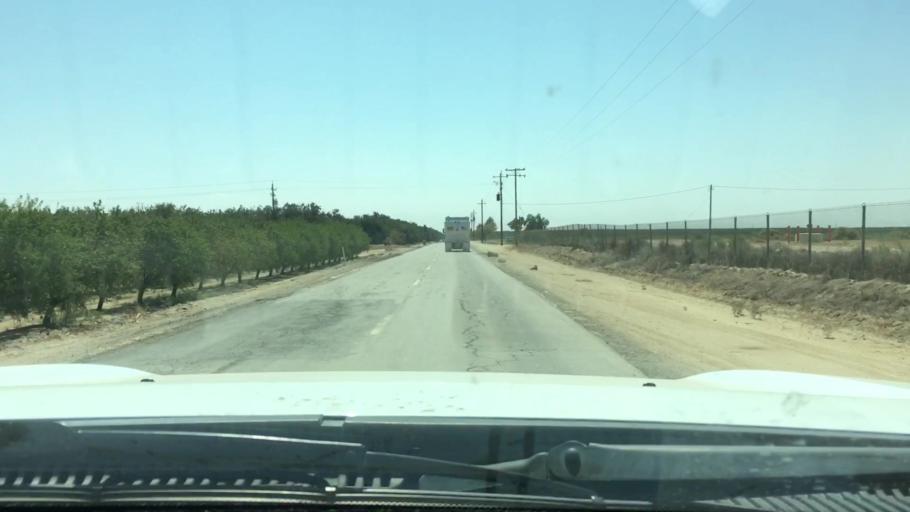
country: US
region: California
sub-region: Kern County
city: Wasco
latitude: 35.5088
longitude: -119.4033
